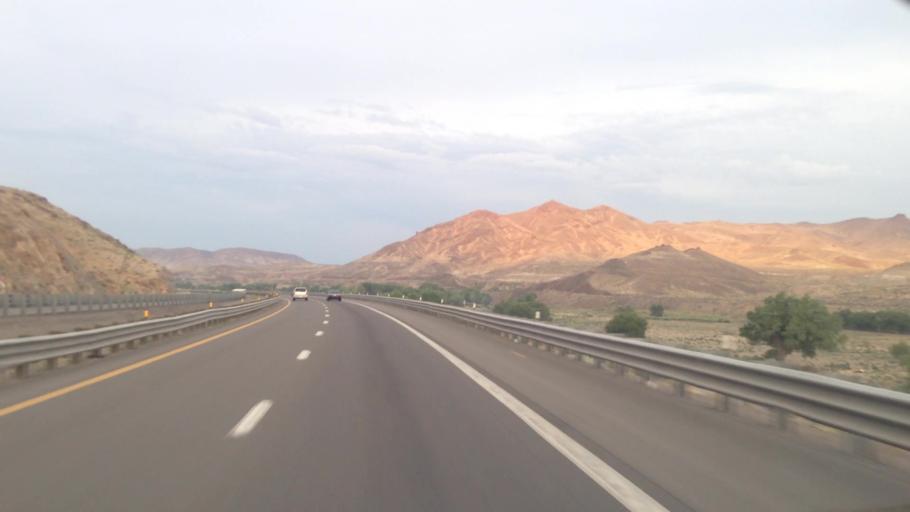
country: US
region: Nevada
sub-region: Lyon County
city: Fernley
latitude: 39.5981
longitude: -119.3537
